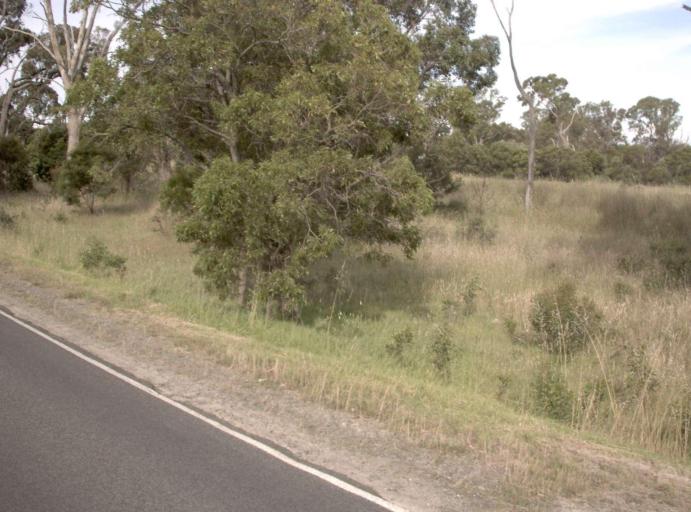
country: AU
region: Victoria
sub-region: Latrobe
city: Traralgon
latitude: -38.0641
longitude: 146.6194
